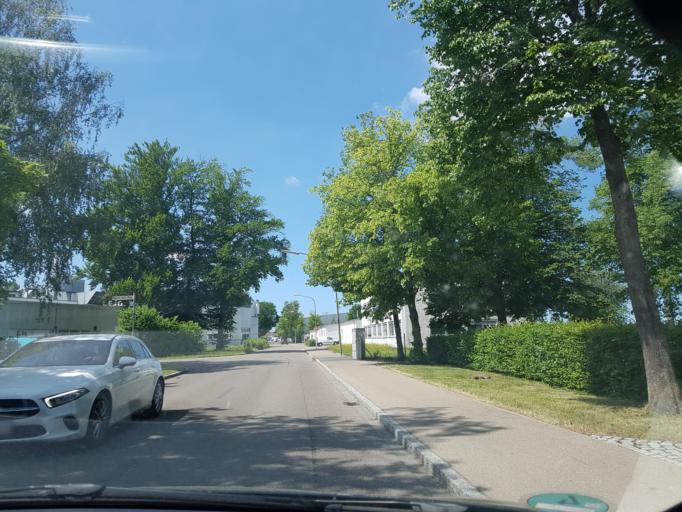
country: DE
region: Bavaria
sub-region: Swabia
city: Nersingen
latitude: 48.4161
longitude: 10.1522
